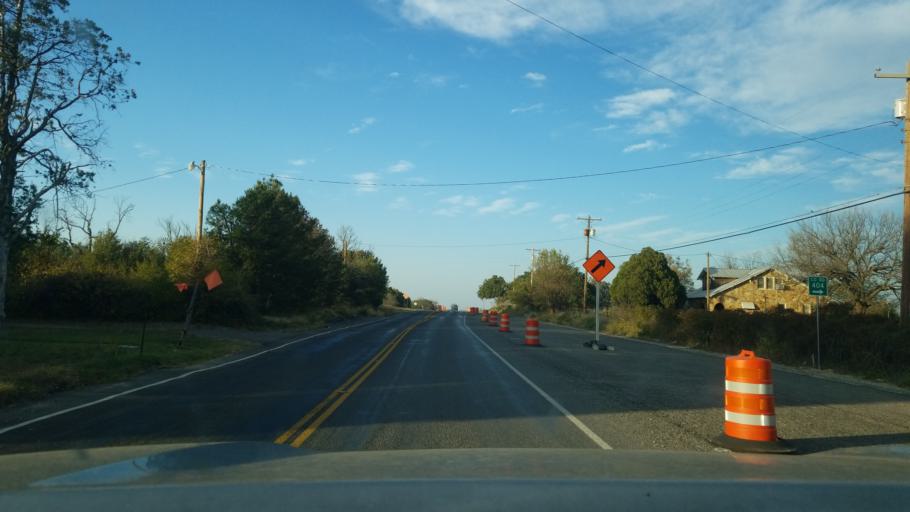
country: US
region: Texas
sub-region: Brown County
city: Lake Brownwood
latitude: 32.1082
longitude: -98.9643
